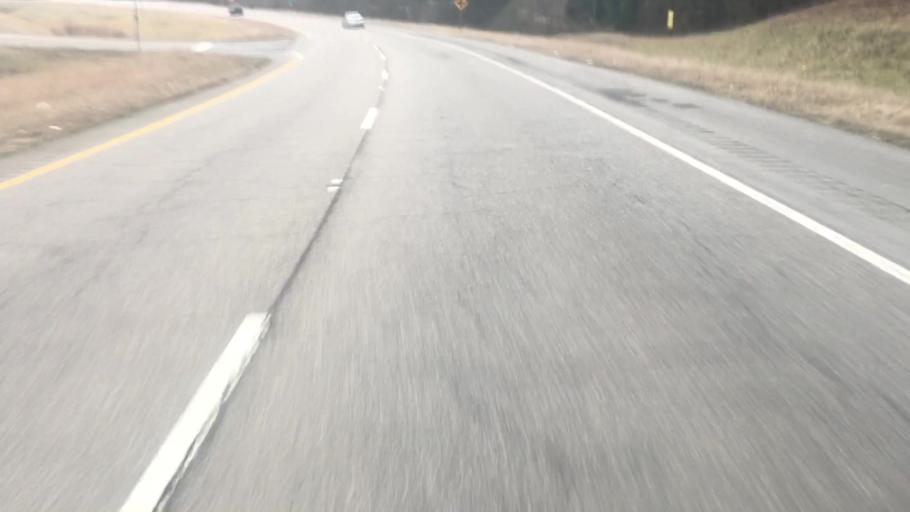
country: US
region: Alabama
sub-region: Walker County
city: Cordova
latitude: 33.8084
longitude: -87.1462
